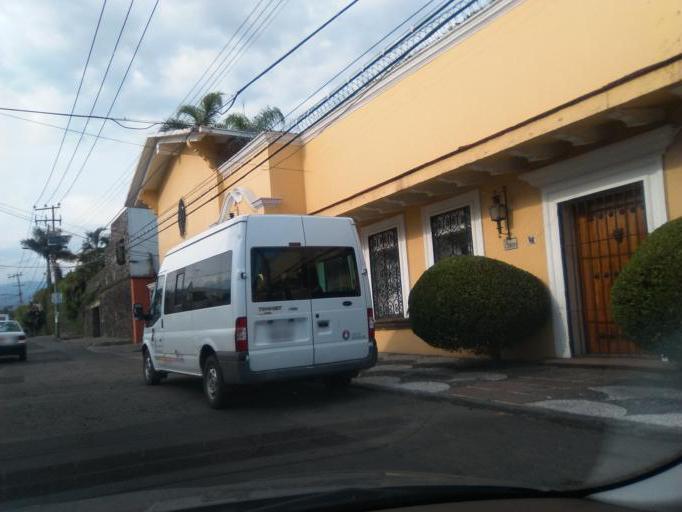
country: MX
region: Morelos
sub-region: Cuernavaca
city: Cuernavaca
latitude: 18.9097
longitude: -99.2283
